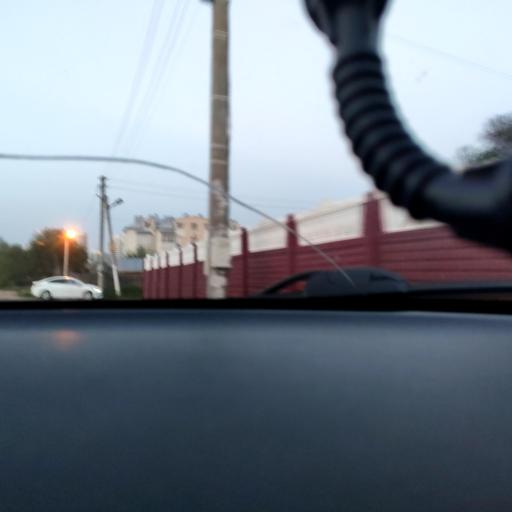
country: RU
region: Tatarstan
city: Osinovo
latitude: 55.8566
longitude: 48.8848
